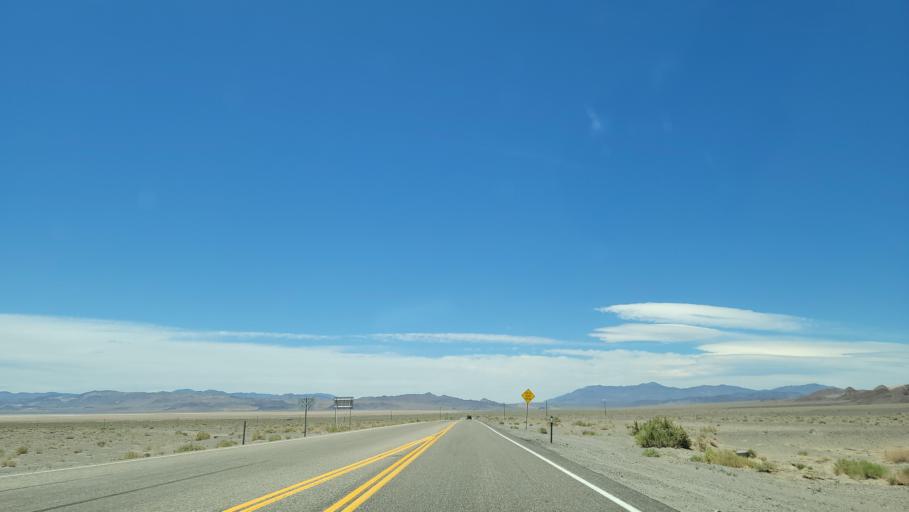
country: US
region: Nevada
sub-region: Nye County
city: Tonopah
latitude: 38.0324
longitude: -117.8874
